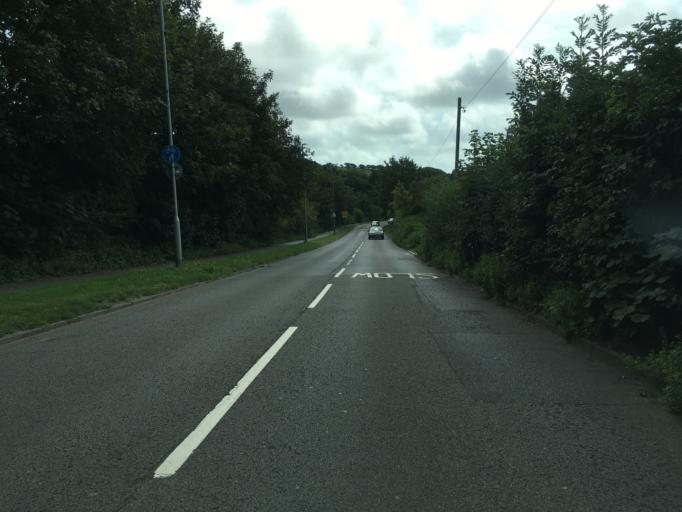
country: GB
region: England
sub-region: Brighton and Hove
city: Rottingdean
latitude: 50.8260
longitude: -0.0696
